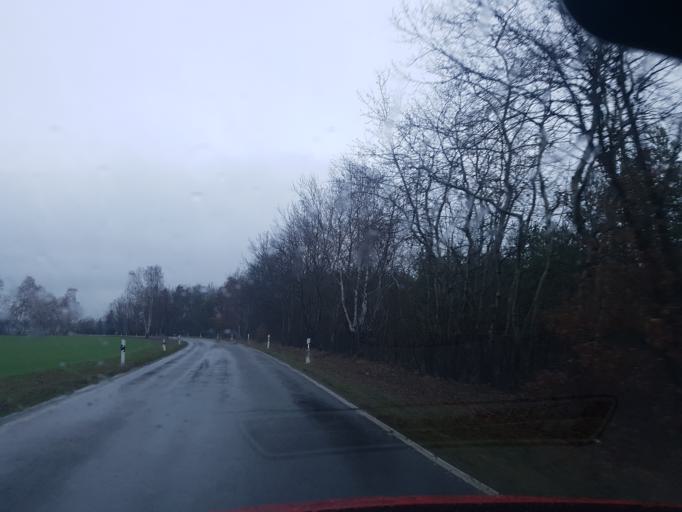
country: DE
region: Brandenburg
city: Schilda
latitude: 51.6228
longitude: 13.3189
